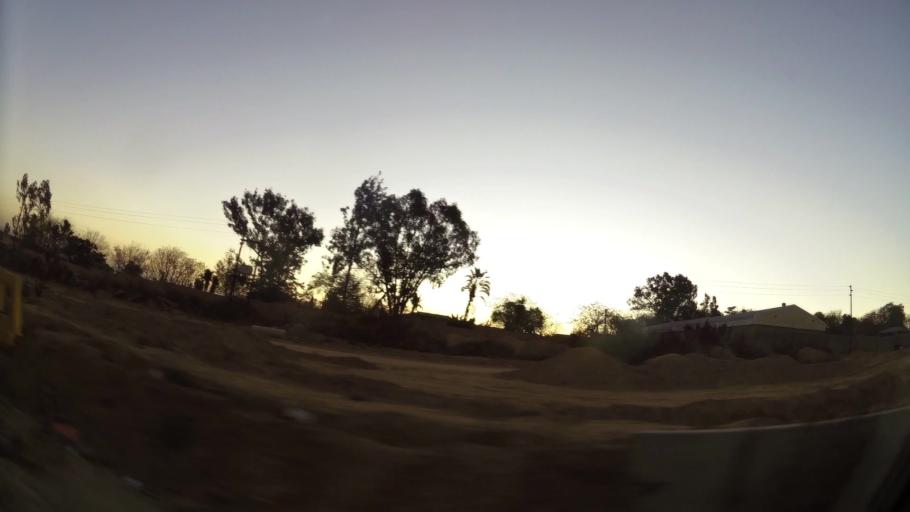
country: ZA
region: Gauteng
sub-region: City of Johannesburg Metropolitan Municipality
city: Diepsloot
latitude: -25.9489
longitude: 28.0188
